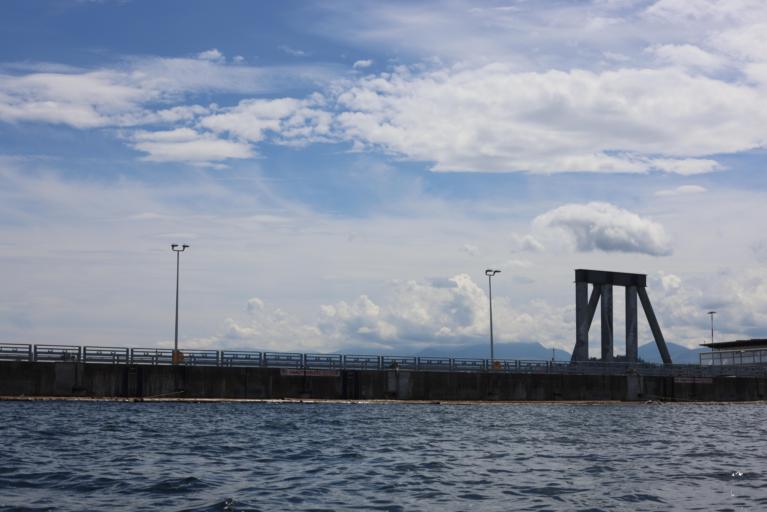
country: CA
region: British Columbia
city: Nanaimo
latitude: 49.1653
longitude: -123.9250
